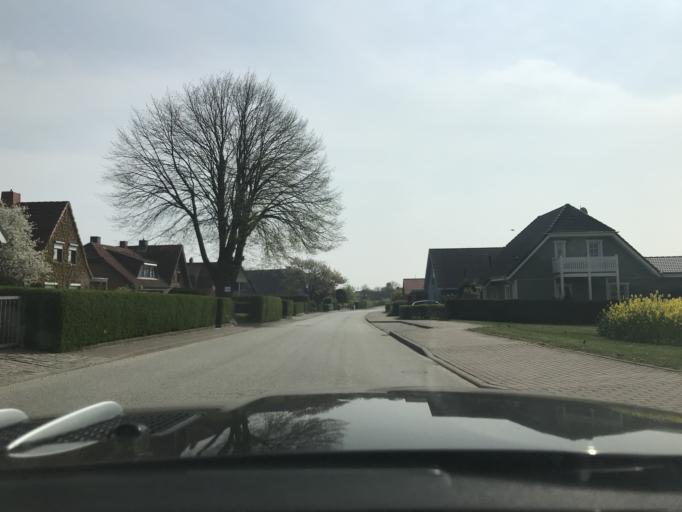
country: DE
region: Schleswig-Holstein
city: Gromitz
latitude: 54.1692
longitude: 10.9749
